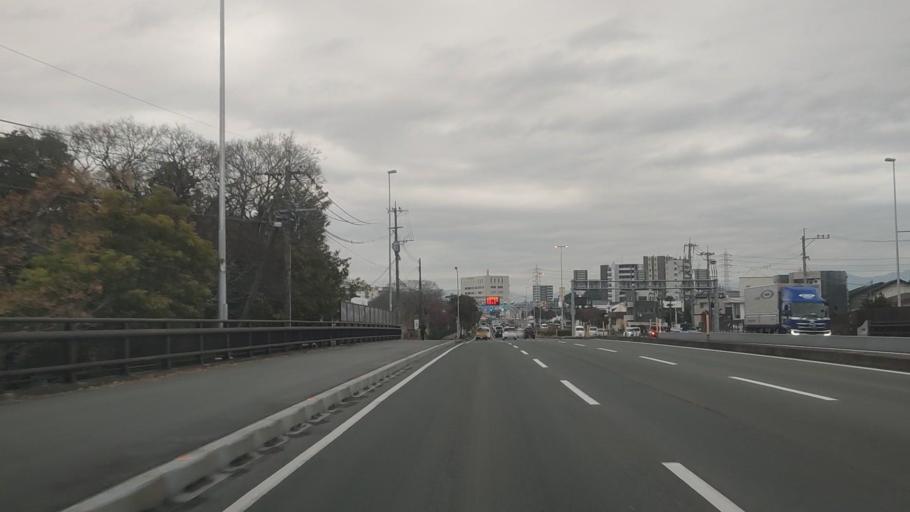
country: JP
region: Kumamoto
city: Kumamoto
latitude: 32.7772
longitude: 130.7396
